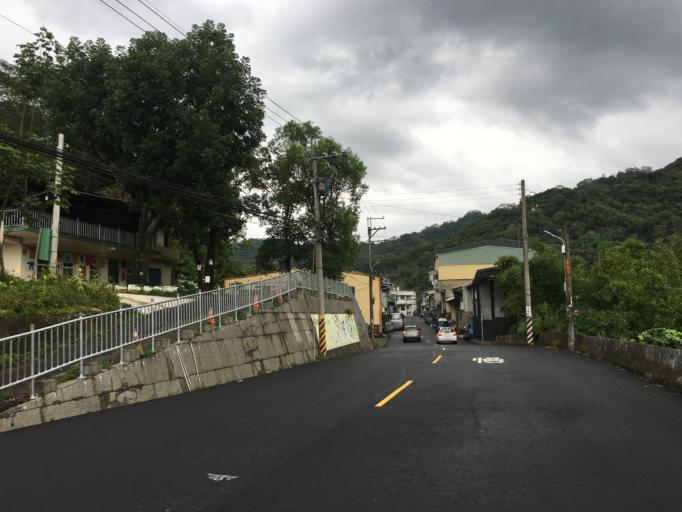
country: TW
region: Taiwan
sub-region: Taichung City
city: Taichung
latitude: 24.0637
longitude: 120.7372
